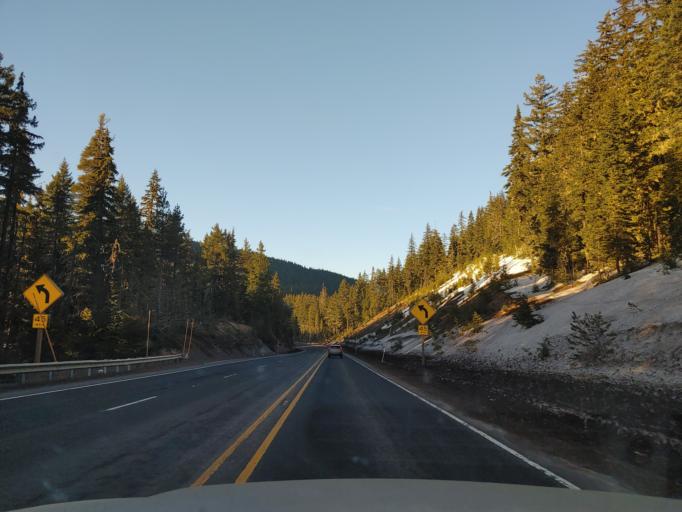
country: US
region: Oregon
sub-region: Lane County
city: Oakridge
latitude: 43.6168
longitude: -122.0689
